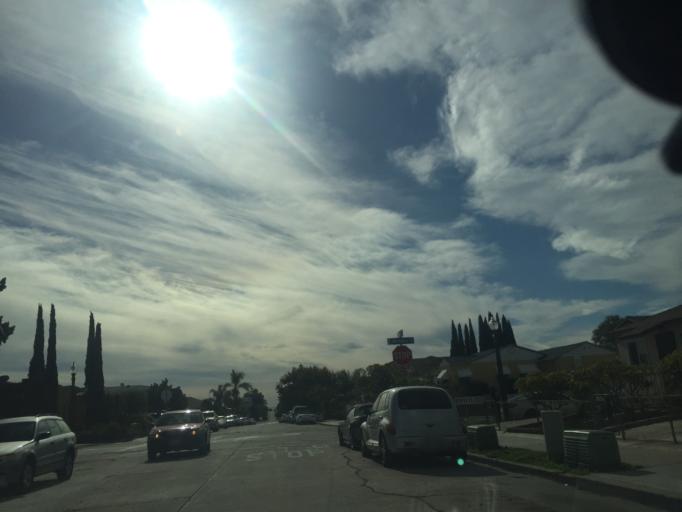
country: US
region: California
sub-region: San Diego County
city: Lemon Grove
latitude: 32.7593
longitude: -117.0836
